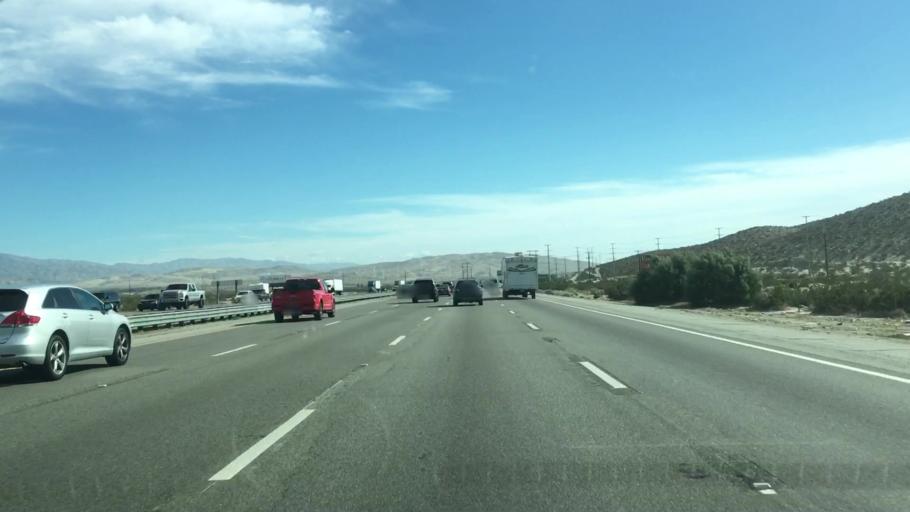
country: US
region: California
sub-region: Riverside County
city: Garnet
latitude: 33.9021
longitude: -116.5366
